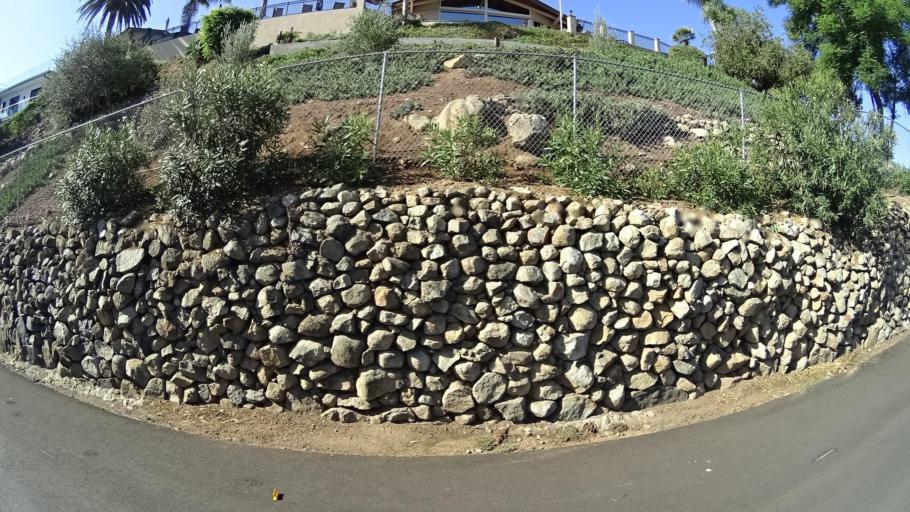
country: US
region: California
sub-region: San Diego County
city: Casa de Oro-Mount Helix
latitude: 32.7708
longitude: -116.9810
